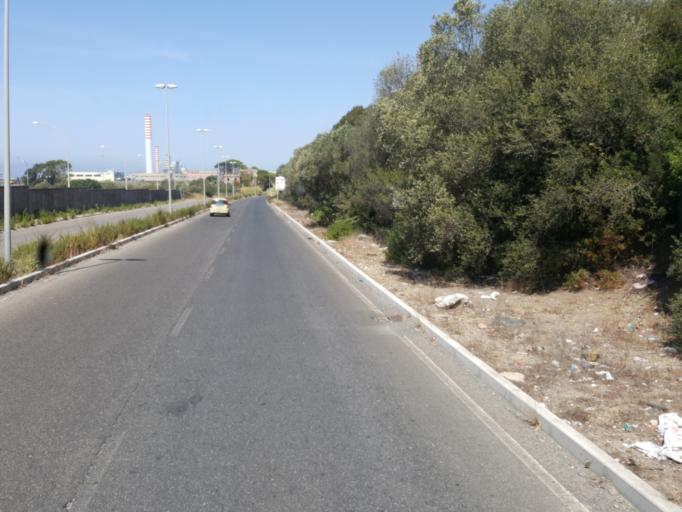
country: IT
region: Latium
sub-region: Citta metropolitana di Roma Capitale
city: Civitavecchia
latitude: 42.1121
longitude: 11.7822
